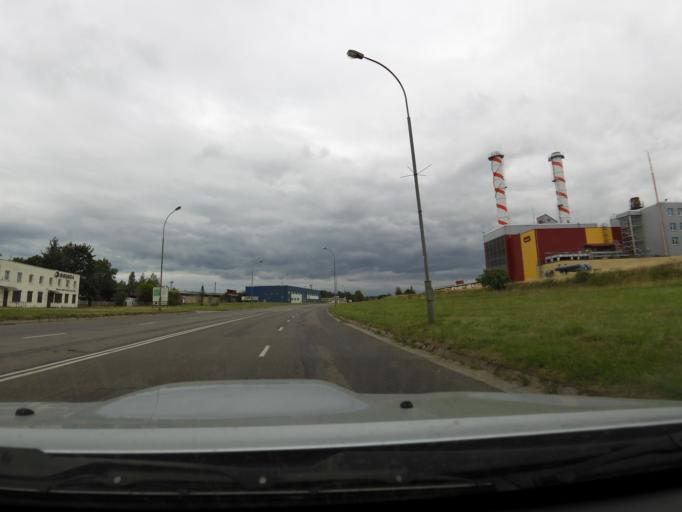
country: LT
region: Panevezys
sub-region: Panevezys City
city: Panevezys
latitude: 55.7477
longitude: 24.3818
